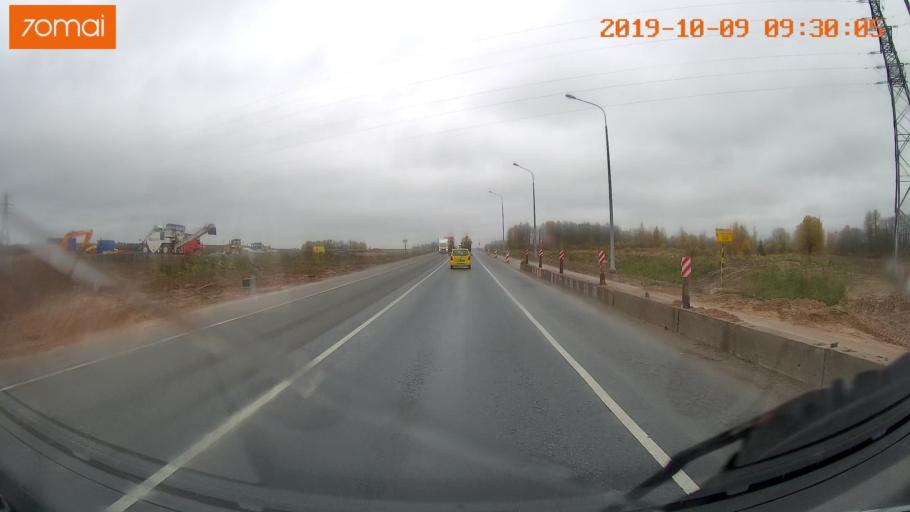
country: RU
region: Vologda
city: Vologda
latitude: 59.1371
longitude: 39.9522
